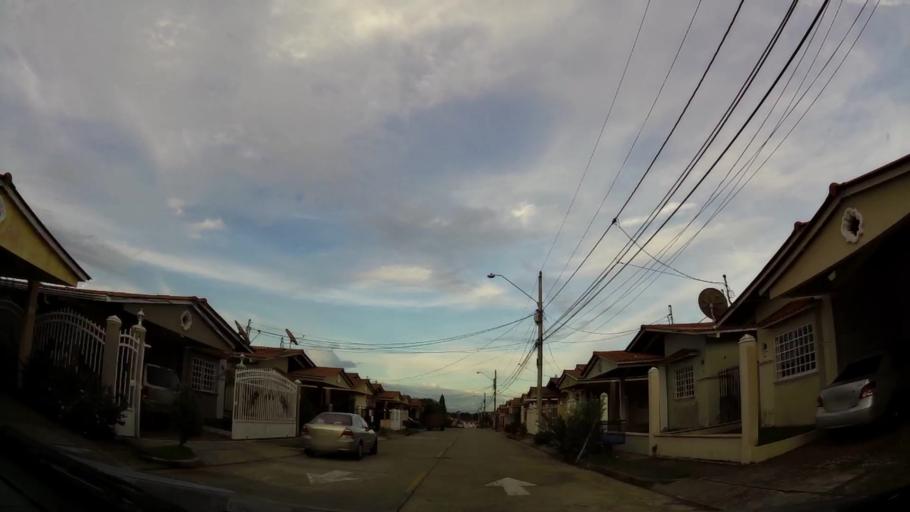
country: PA
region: Panama
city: La Chorrera
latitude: 8.8682
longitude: -79.7661
